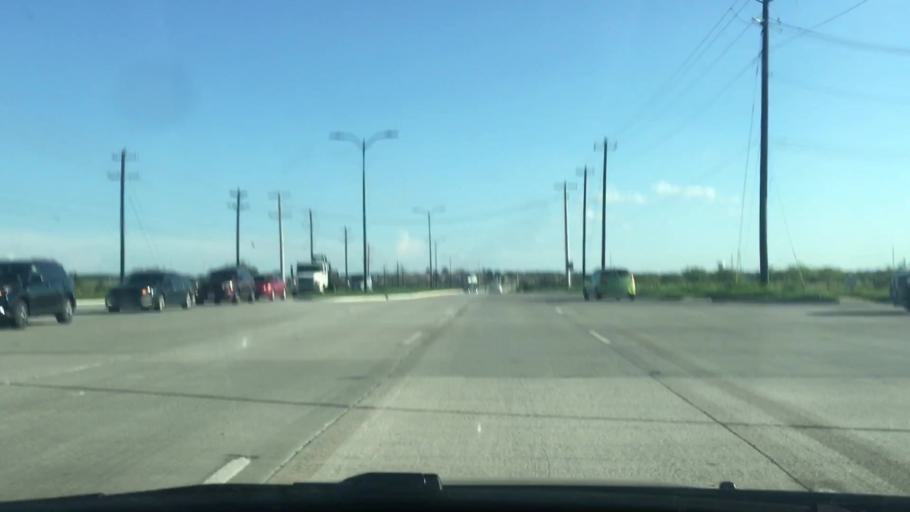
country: US
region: Texas
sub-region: Denton County
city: Little Elm
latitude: 33.2110
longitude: -96.8805
